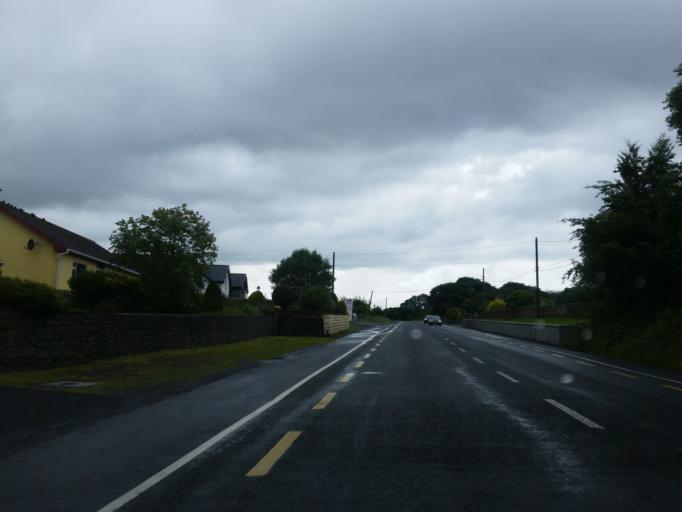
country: IE
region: Connaught
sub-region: Sligo
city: Strandhill
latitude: 54.2727
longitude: -8.5502
